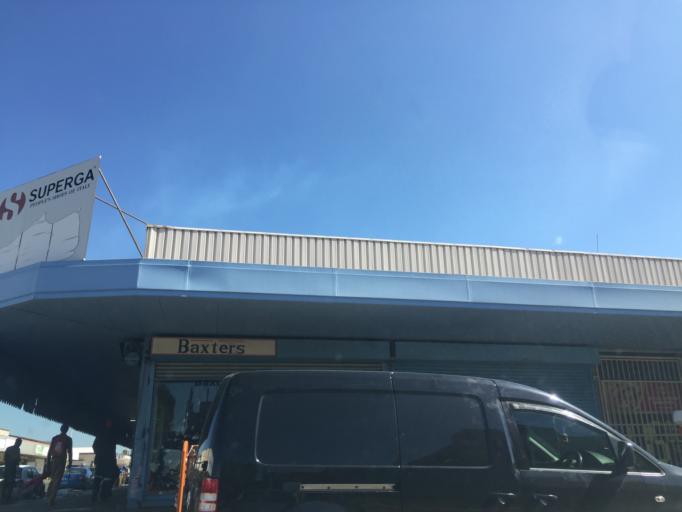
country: ZA
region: Gauteng
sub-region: Sedibeng District Municipality
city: Vanderbijlpark
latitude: -26.6977
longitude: 27.8377
